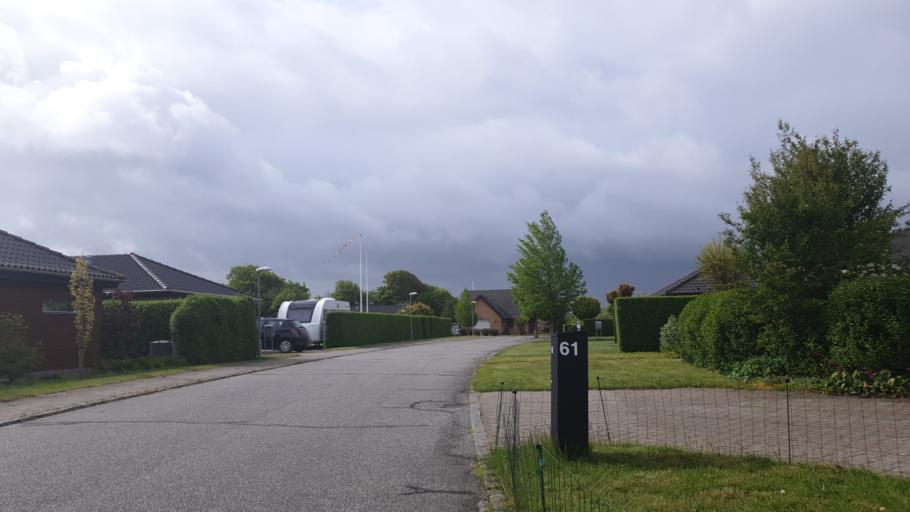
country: DK
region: Central Jutland
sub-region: Hedensted Kommune
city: Hedensted
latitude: 55.7918
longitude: 9.6922
